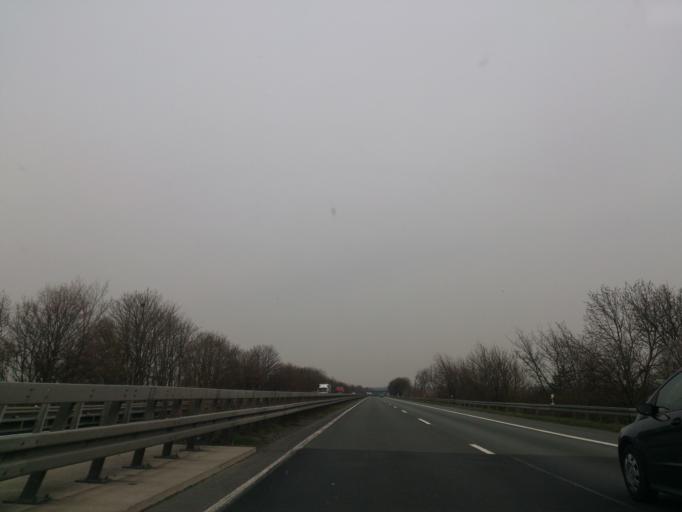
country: DE
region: North Rhine-Westphalia
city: Erwitte
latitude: 51.5883
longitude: 8.3962
